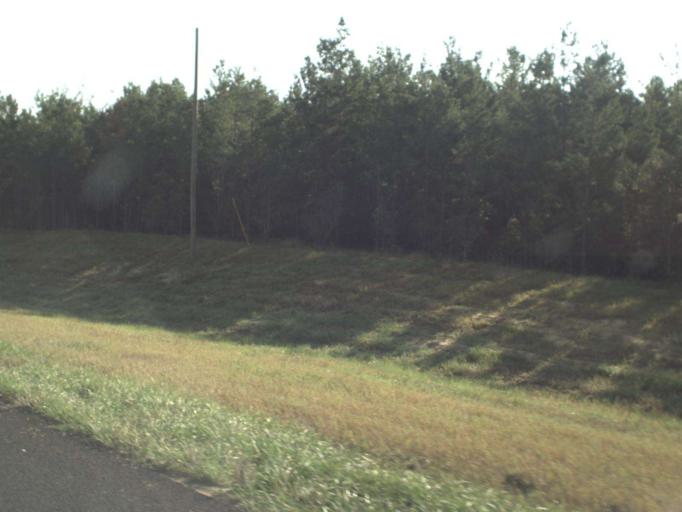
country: US
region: Florida
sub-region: Holmes County
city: Bonifay
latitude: 30.5639
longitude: -85.8095
